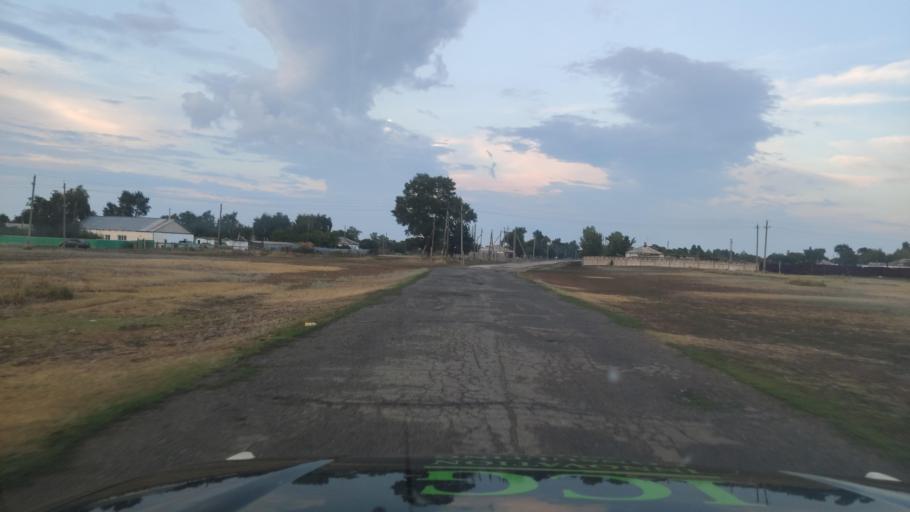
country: KZ
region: Pavlodar
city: Pavlodar
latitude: 52.2337
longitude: 77.5890
